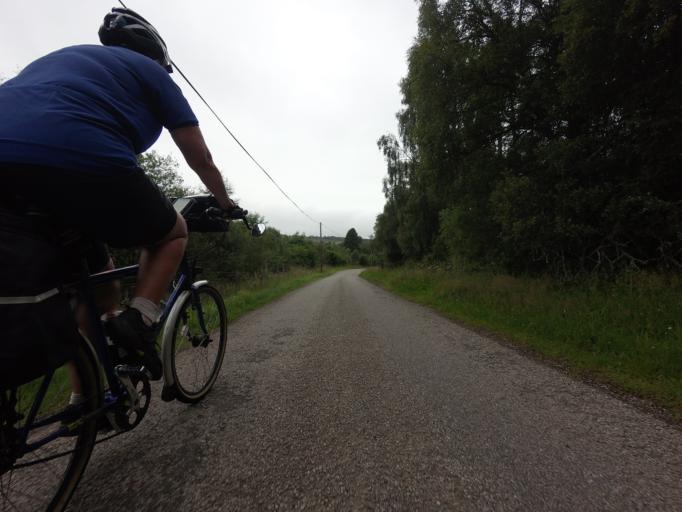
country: GB
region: Scotland
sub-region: Highland
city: Evanton
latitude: 57.9863
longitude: -4.4147
